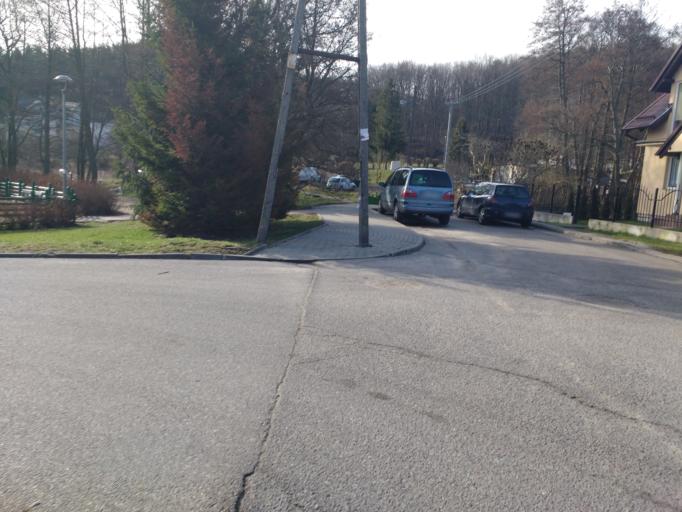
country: PL
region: Pomeranian Voivodeship
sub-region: Gdynia
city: Wielki Kack
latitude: 54.4842
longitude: 18.5154
